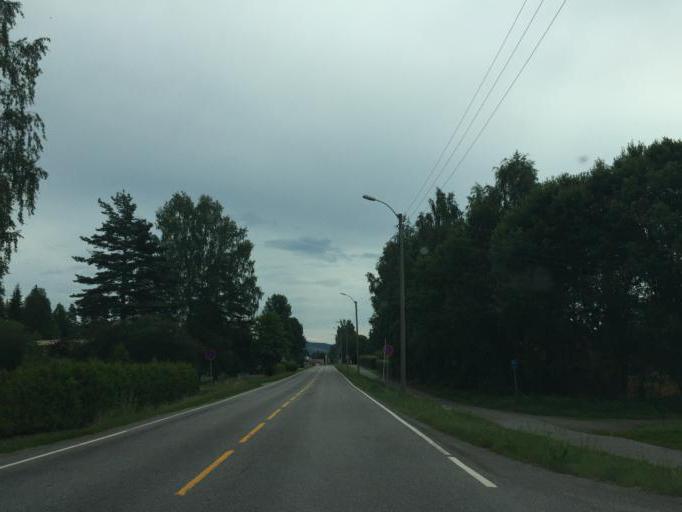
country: NO
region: Hedmark
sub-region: Kongsvinger
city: Kongsvinger
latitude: 60.1988
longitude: 11.9936
